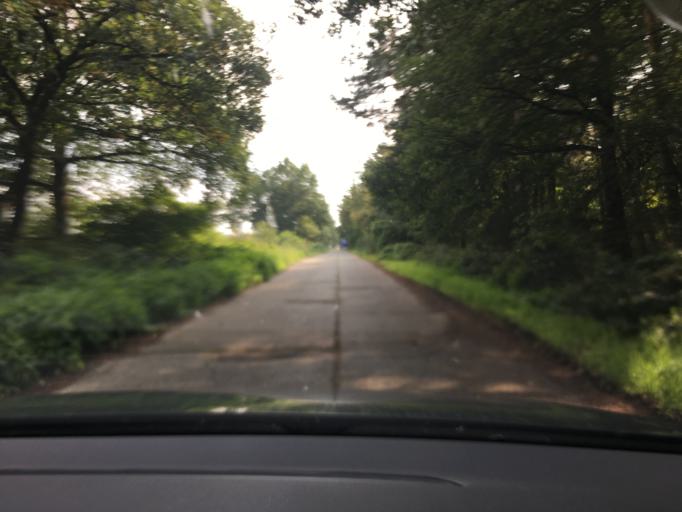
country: DE
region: North Rhine-Westphalia
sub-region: Regierungsbezirk Koln
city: Kreuzau
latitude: 50.7642
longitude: 6.5165
